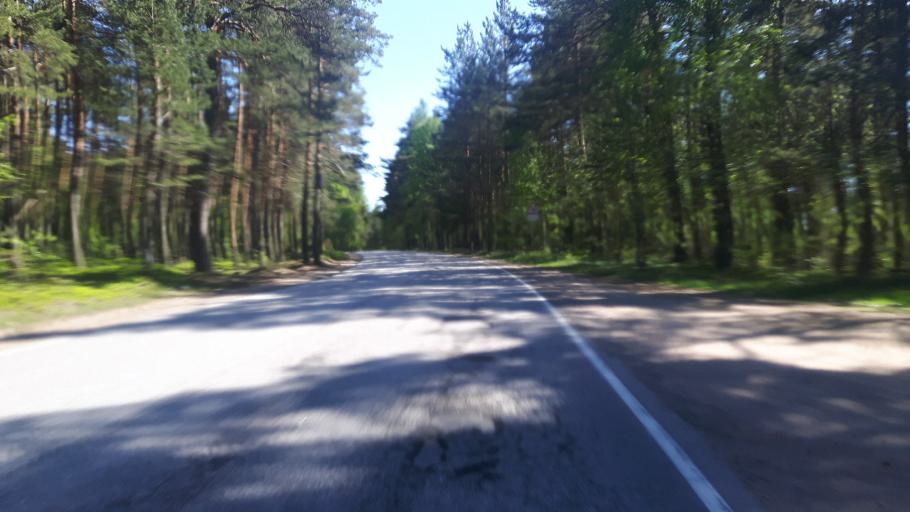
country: RU
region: Leningrad
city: Glebychevo
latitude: 60.2899
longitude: 28.8707
